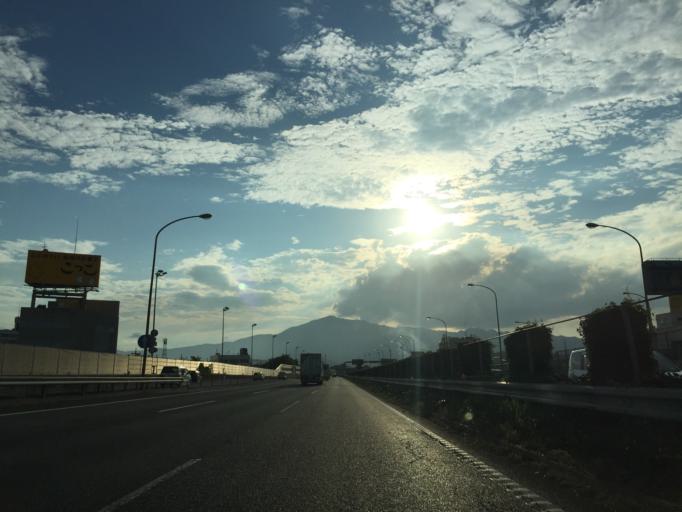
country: JP
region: Kanagawa
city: Atsugi
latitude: 35.4240
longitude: 139.3614
